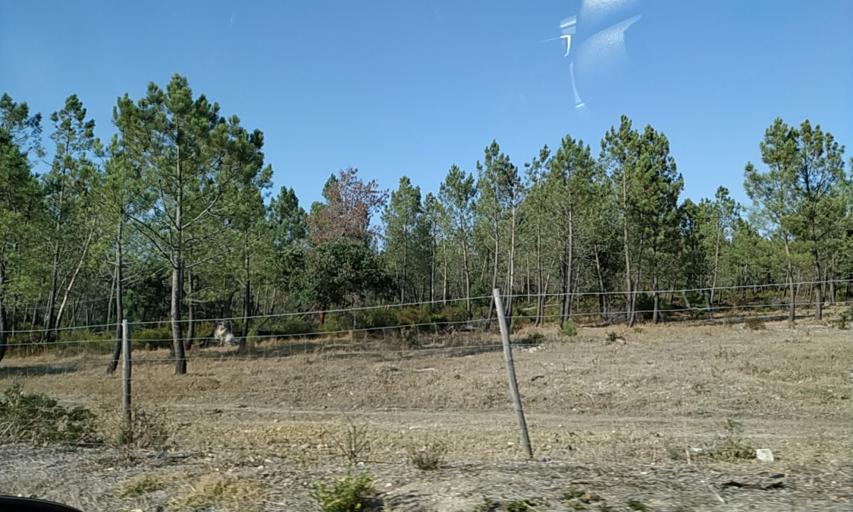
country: PT
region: Santarem
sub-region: Almeirim
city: Fazendas de Almeirim
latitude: 39.1256
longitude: -8.6034
